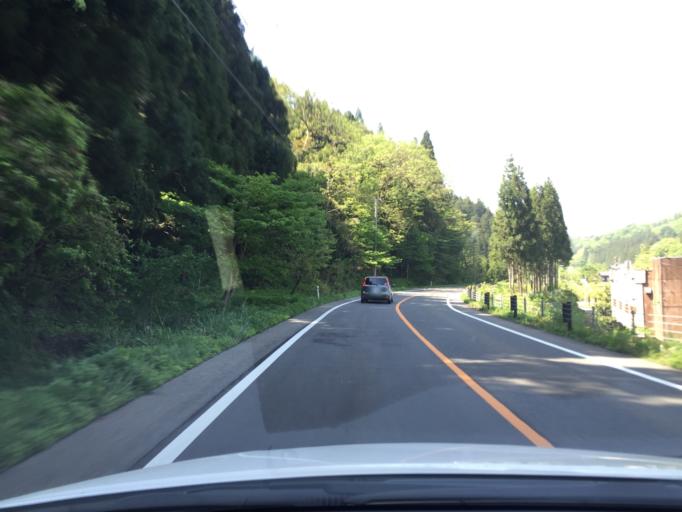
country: JP
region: Niigata
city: Muramatsu
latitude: 37.6519
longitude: 139.1354
